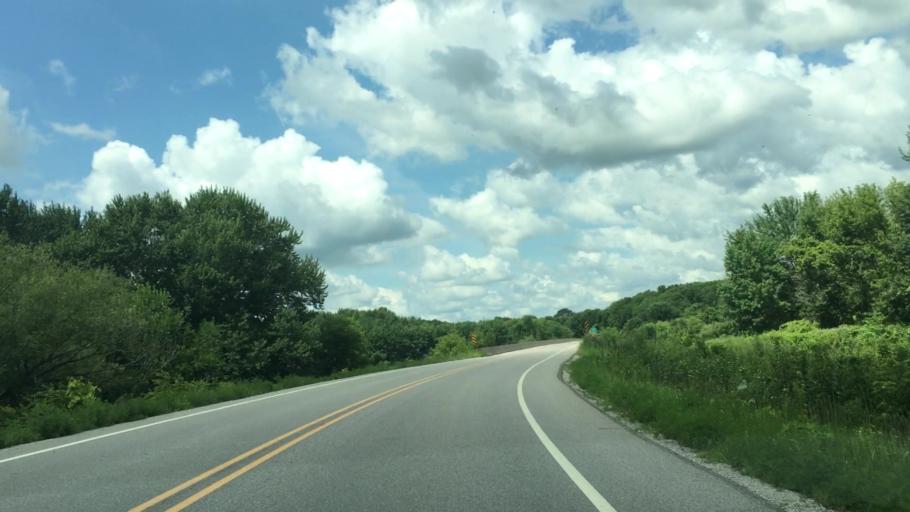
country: US
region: Iowa
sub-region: Linn County
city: Lisbon
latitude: 41.8451
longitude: -91.3883
